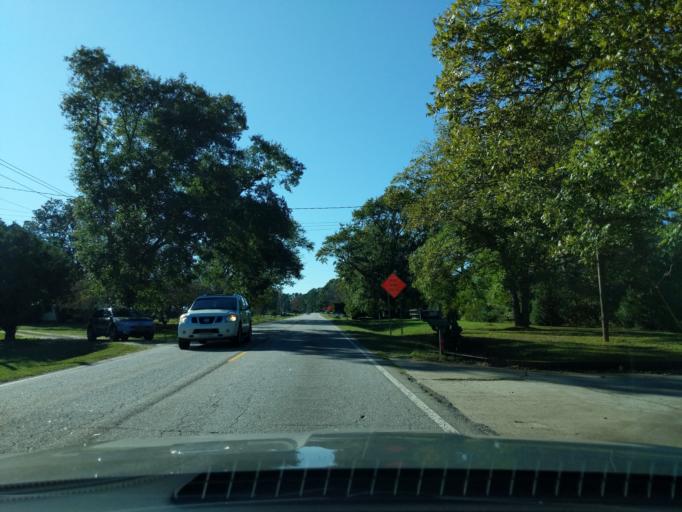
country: US
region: Georgia
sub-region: Columbia County
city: Grovetown
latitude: 33.4655
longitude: -82.1690
